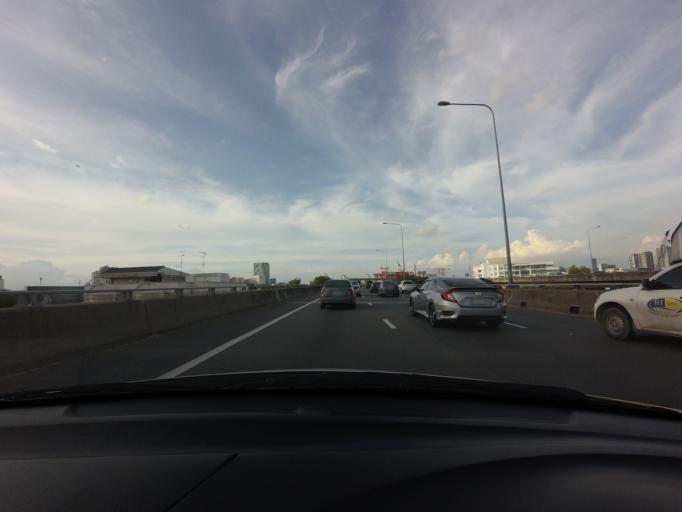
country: TH
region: Bangkok
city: Bang Sue
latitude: 13.7967
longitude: 100.5391
